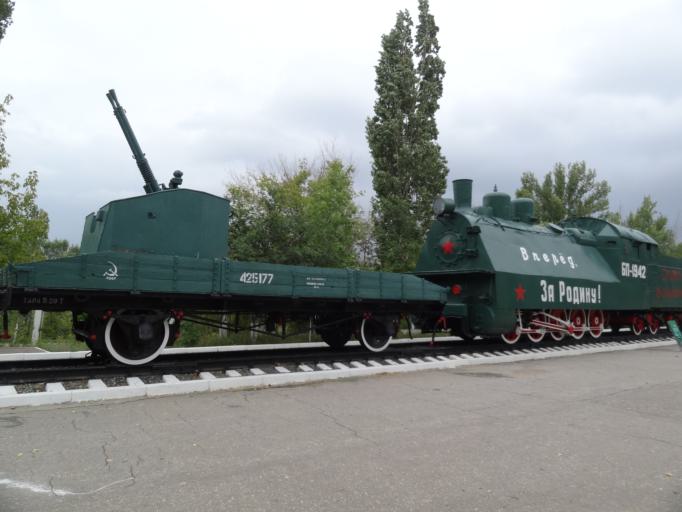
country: RU
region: Saratov
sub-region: Saratovskiy Rayon
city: Saratov
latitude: 51.5467
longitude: 46.0531
